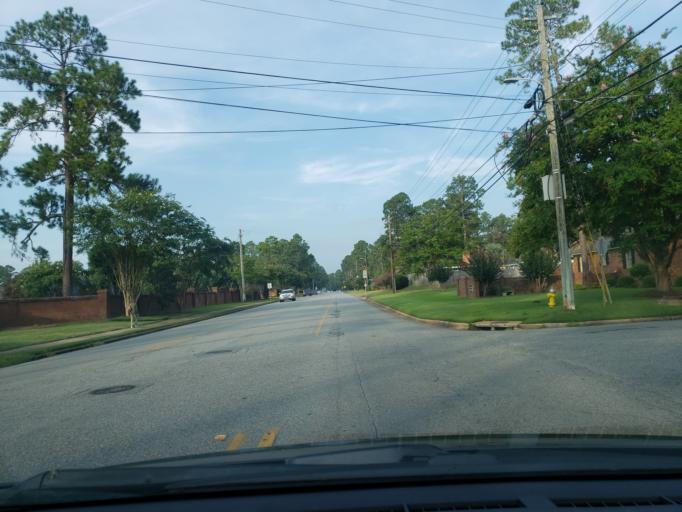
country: US
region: Georgia
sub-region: Dougherty County
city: Albany
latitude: 31.6032
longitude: -84.2107
